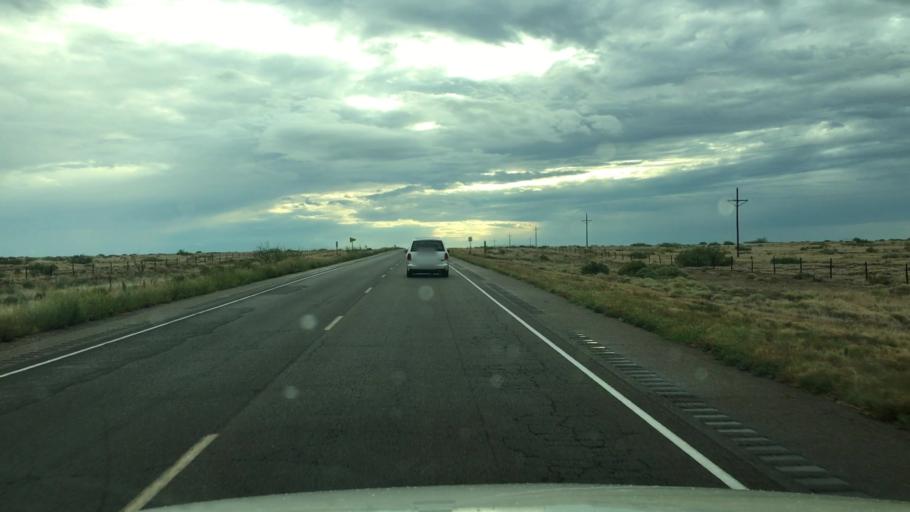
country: US
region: New Mexico
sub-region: Chaves County
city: Roswell
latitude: 33.4021
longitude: -104.3295
